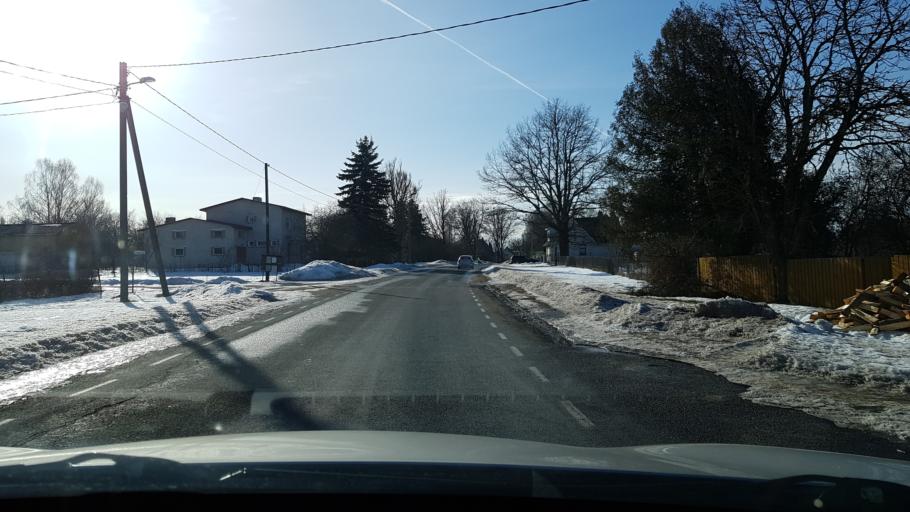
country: EE
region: Viljandimaa
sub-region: Suure-Jaani vald
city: Suure-Jaani
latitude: 58.5415
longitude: 25.4753
